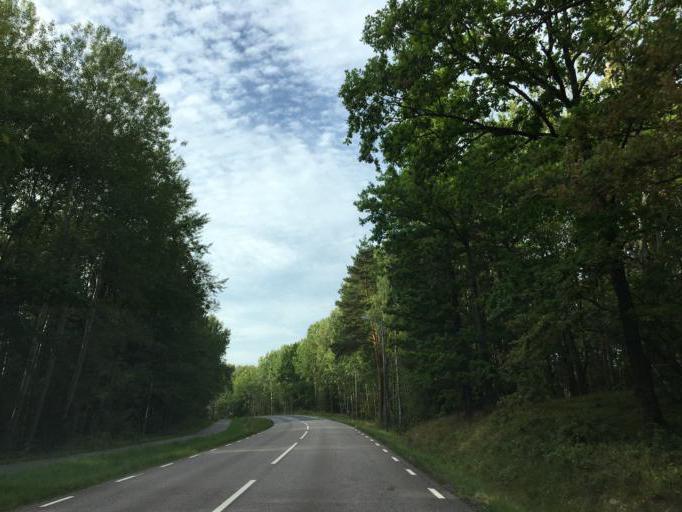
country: SE
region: Soedermanland
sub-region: Eskilstuna Kommun
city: Torshalla
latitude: 59.4466
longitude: 16.4489
